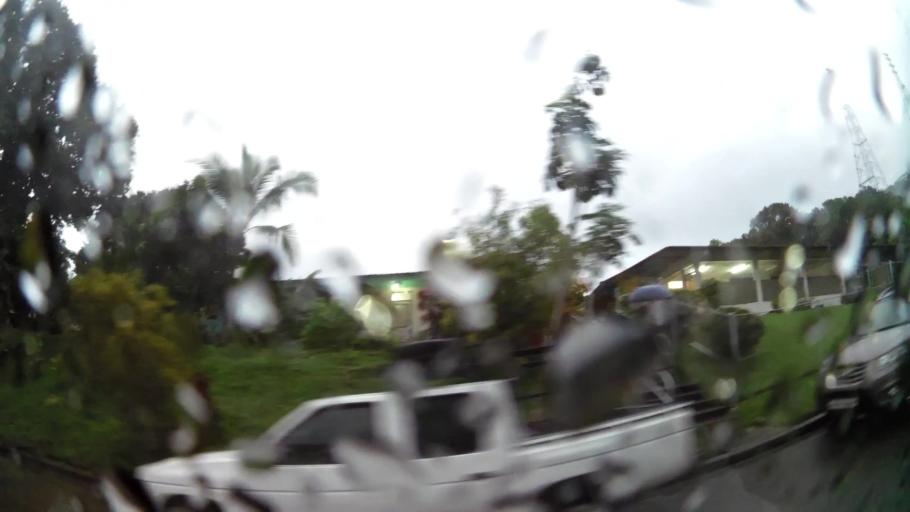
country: PA
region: Panama
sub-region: Distrito de Panama
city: Paraiso
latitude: 9.0332
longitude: -79.6267
